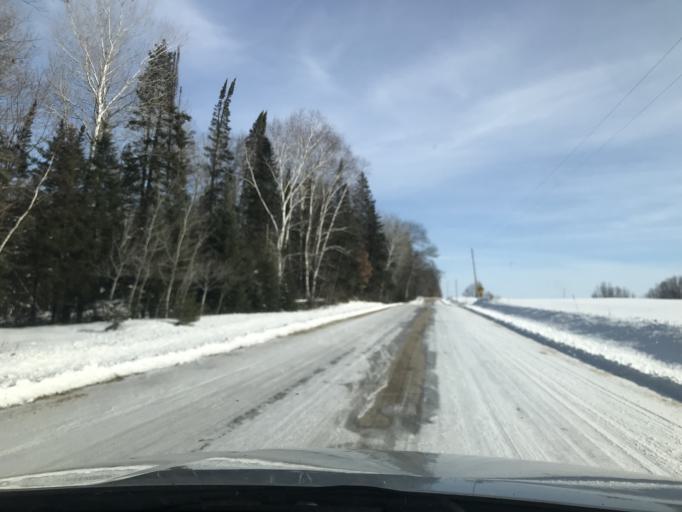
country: US
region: Wisconsin
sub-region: Oconto County
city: Gillett
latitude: 45.1201
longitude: -88.2445
